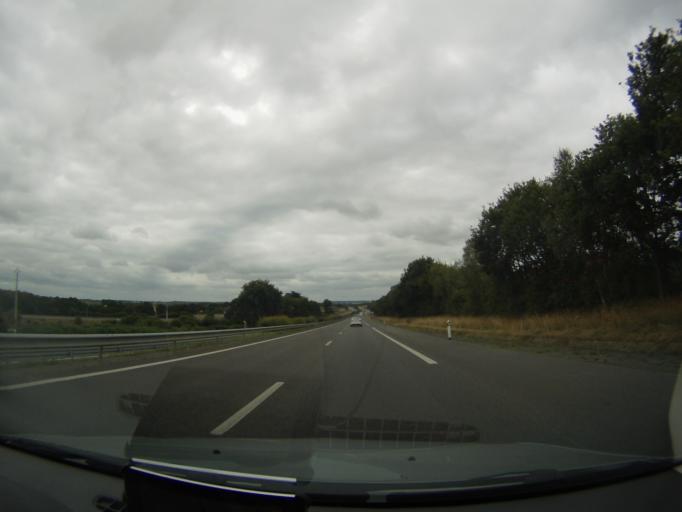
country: FR
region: Brittany
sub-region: Departement d'Ille-et-Vilaine
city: Crevin
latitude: 47.9246
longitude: -1.6770
